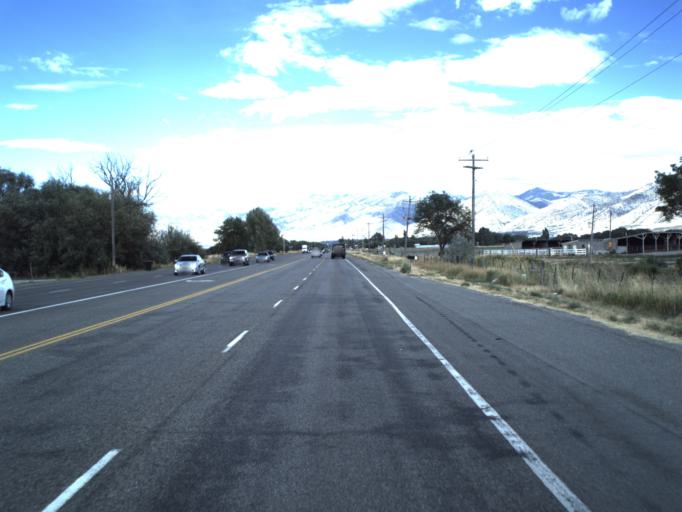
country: US
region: Utah
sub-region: Cache County
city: Hyrum
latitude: 41.6674
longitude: -111.8909
